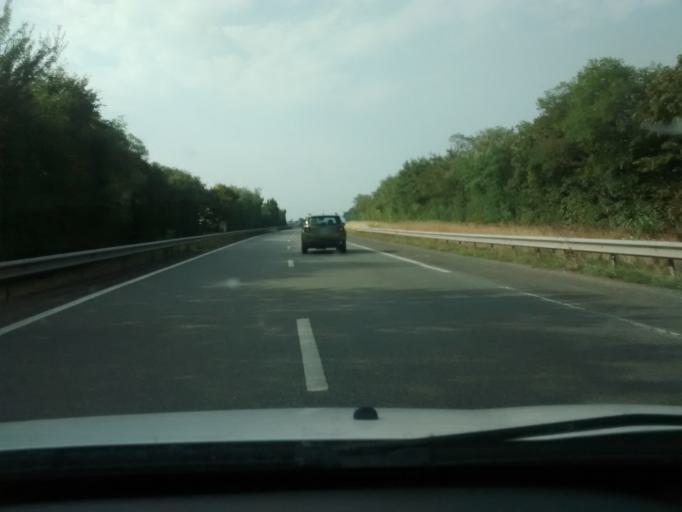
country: FR
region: Brittany
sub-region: Departement d'Ille-et-Vilaine
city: Crevin
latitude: 47.9116
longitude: -1.6826
